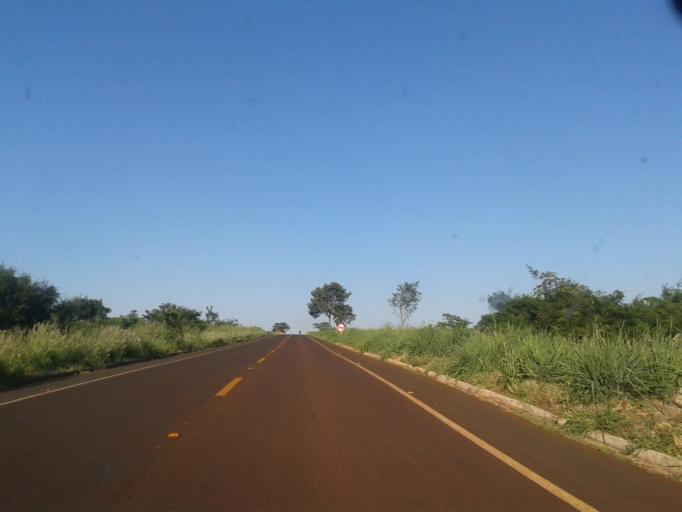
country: BR
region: Minas Gerais
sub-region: Capinopolis
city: Capinopolis
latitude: -18.7119
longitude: -49.7816
